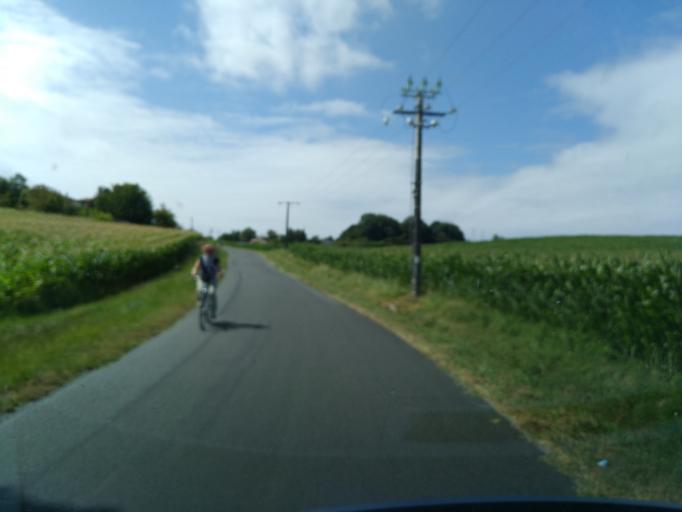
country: FR
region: Poitou-Charentes
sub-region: Departement de la Charente-Maritime
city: Saint-Palais-sur-Mer
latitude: 45.6788
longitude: -1.0870
